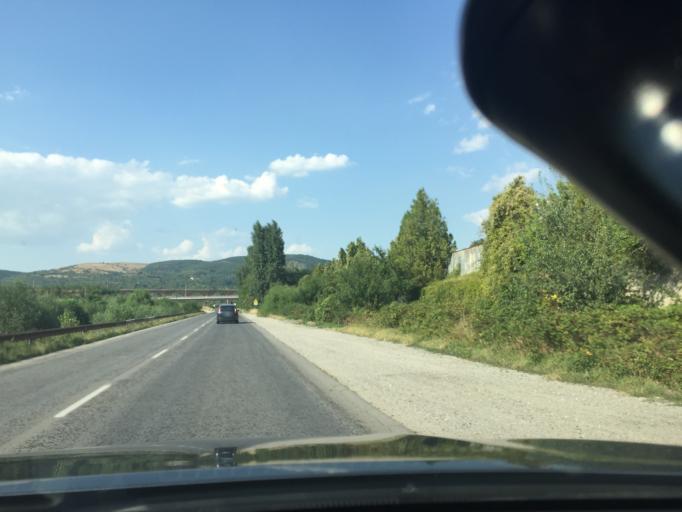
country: BG
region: Kyustendil
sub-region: Obshtina Dupnitsa
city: Dupnitsa
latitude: 42.2497
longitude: 23.0937
